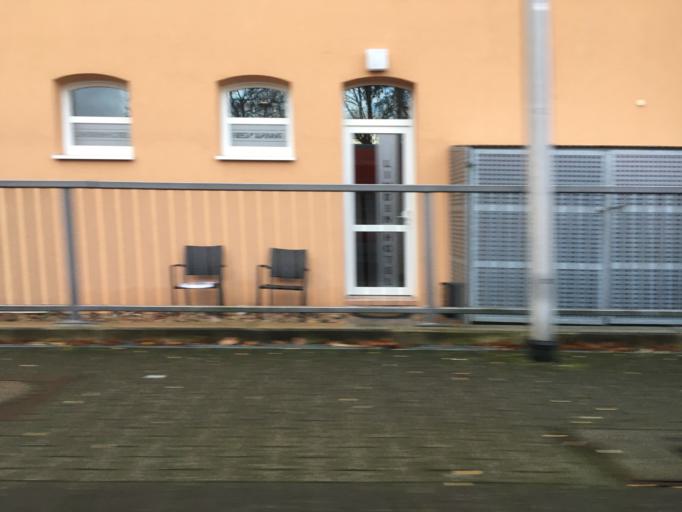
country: DE
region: North Rhine-Westphalia
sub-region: Regierungsbezirk Munster
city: Altenberge
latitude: 52.0524
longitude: 7.4811
